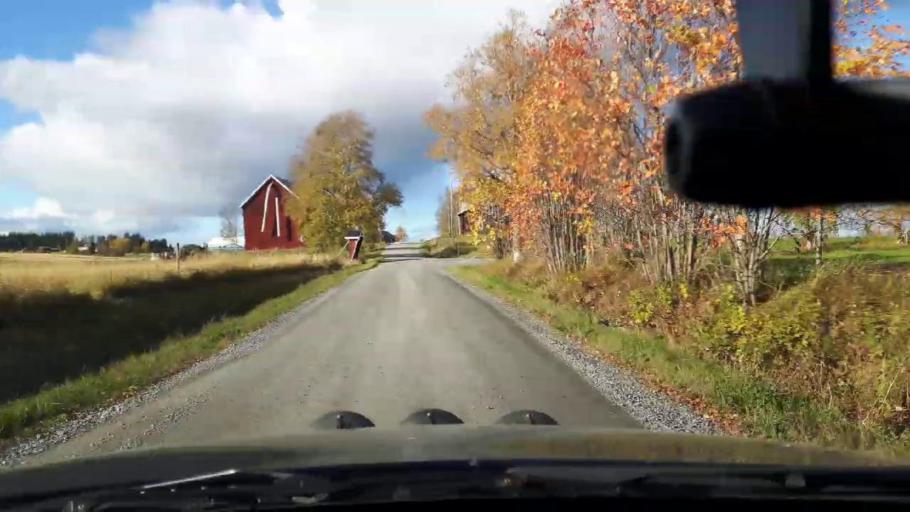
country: SE
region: Jaemtland
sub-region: Bergs Kommun
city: Hoverberg
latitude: 63.0587
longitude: 14.2364
